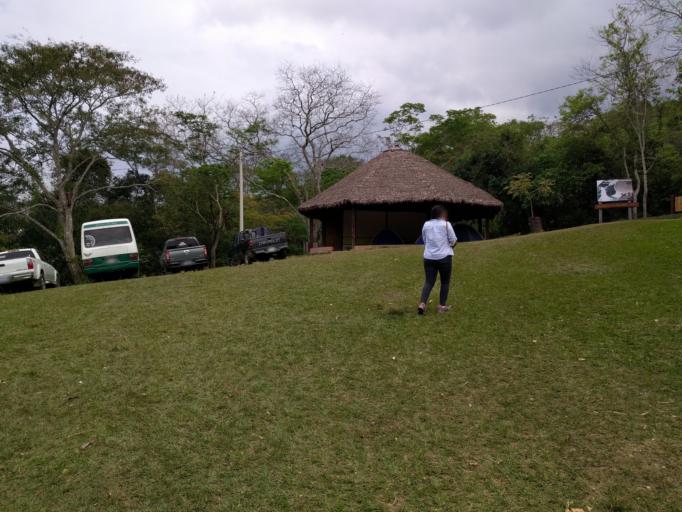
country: BO
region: Santa Cruz
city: Santiago del Torno
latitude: -17.9010
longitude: -63.4379
